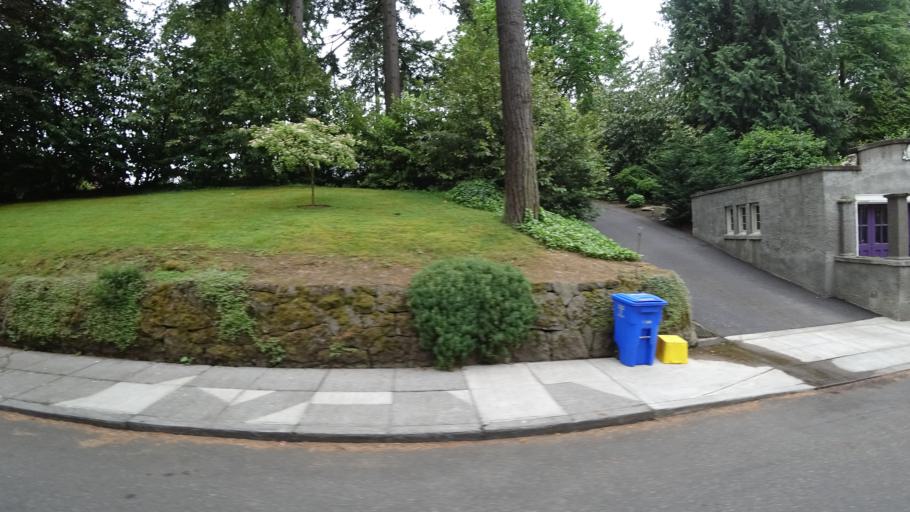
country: US
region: Oregon
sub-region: Multnomah County
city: Portland
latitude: 45.5041
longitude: -122.7013
